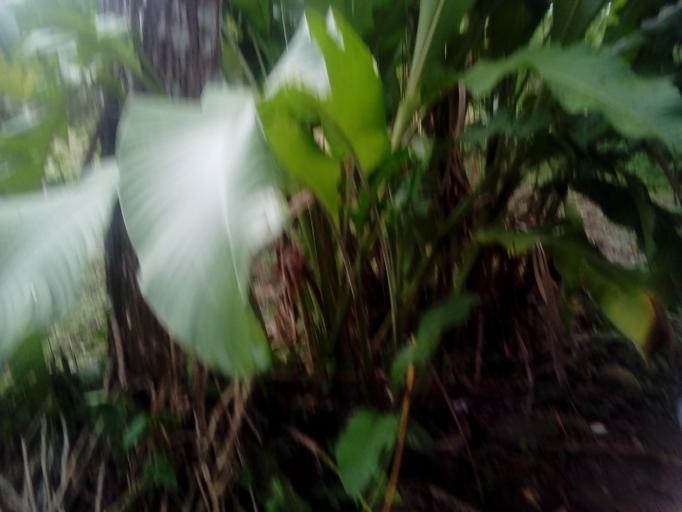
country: CR
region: Alajuela
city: Quesada
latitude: 10.4241
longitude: -84.4587
